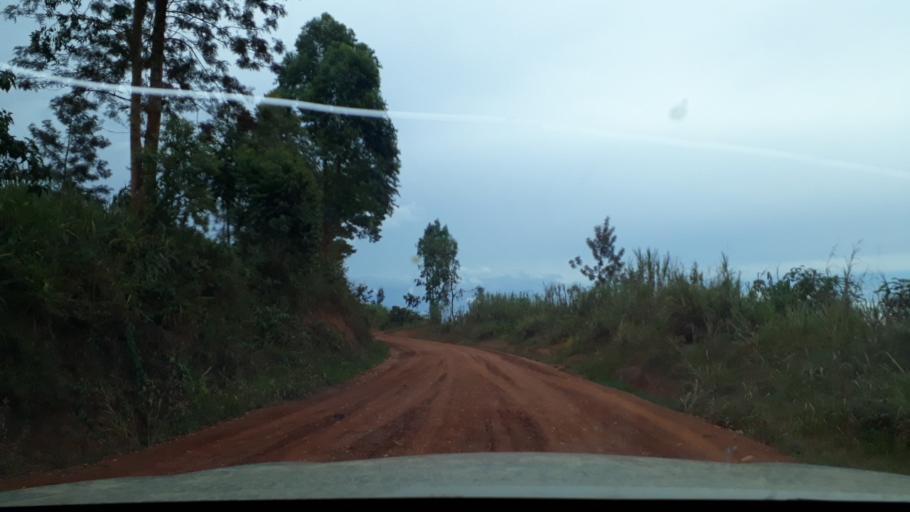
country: CD
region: Eastern Province
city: Bunia
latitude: 1.7726
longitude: 30.3914
